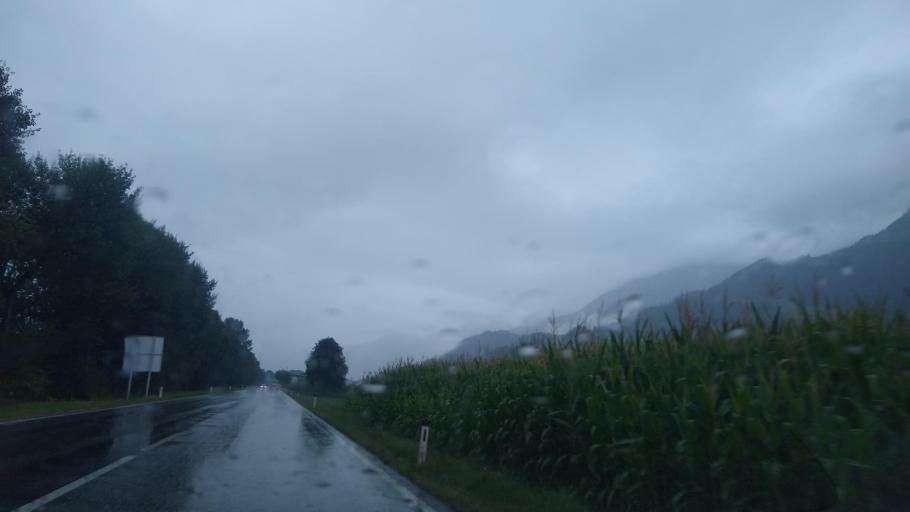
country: AT
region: Tyrol
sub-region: Politischer Bezirk Schwaz
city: Schwaz
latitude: 47.3574
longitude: 11.7145
